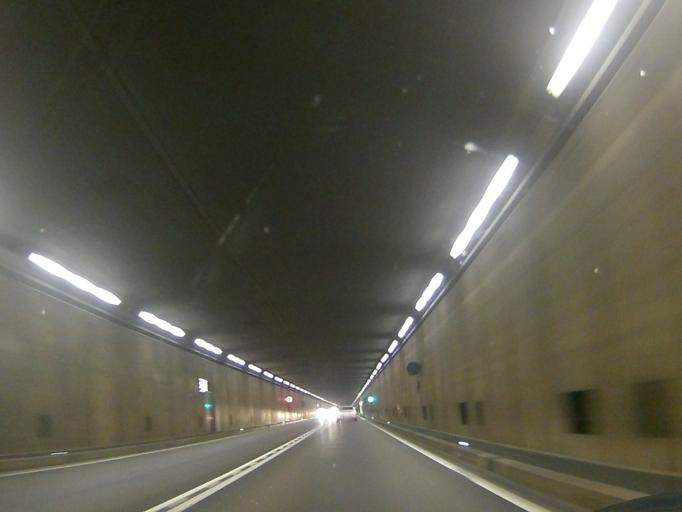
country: CH
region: Uri
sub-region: Uri
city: Andermatt
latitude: 46.5806
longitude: 8.5697
